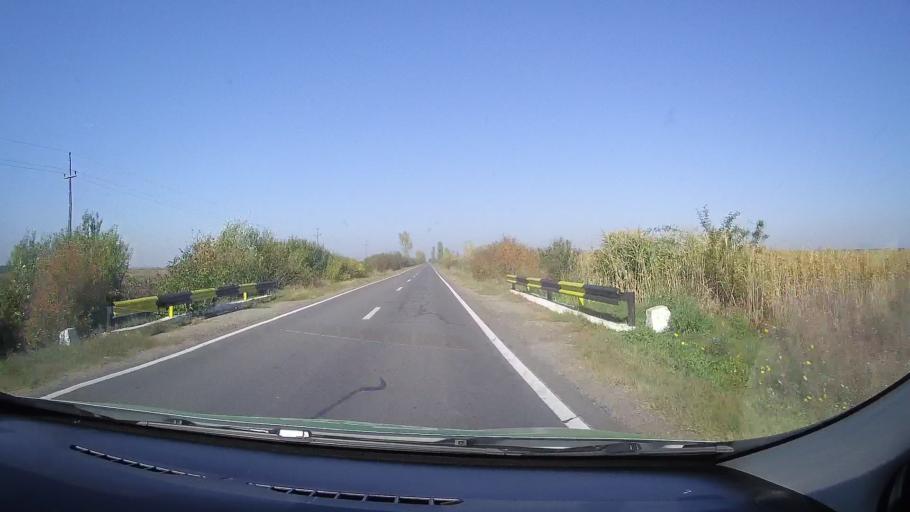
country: RO
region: Satu Mare
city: Carei
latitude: 47.7058
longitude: 22.4328
